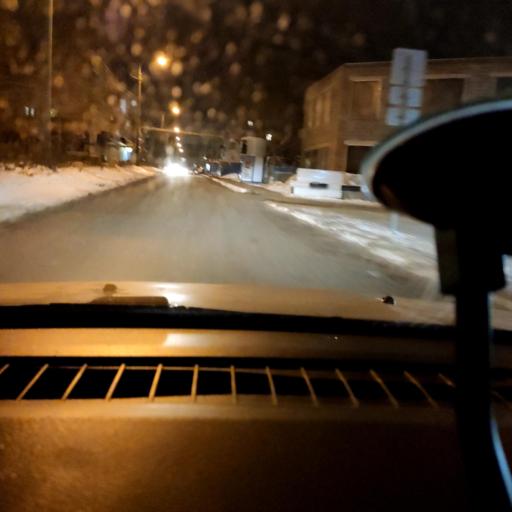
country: RU
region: Samara
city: Volzhskiy
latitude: 53.3490
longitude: 50.2196
